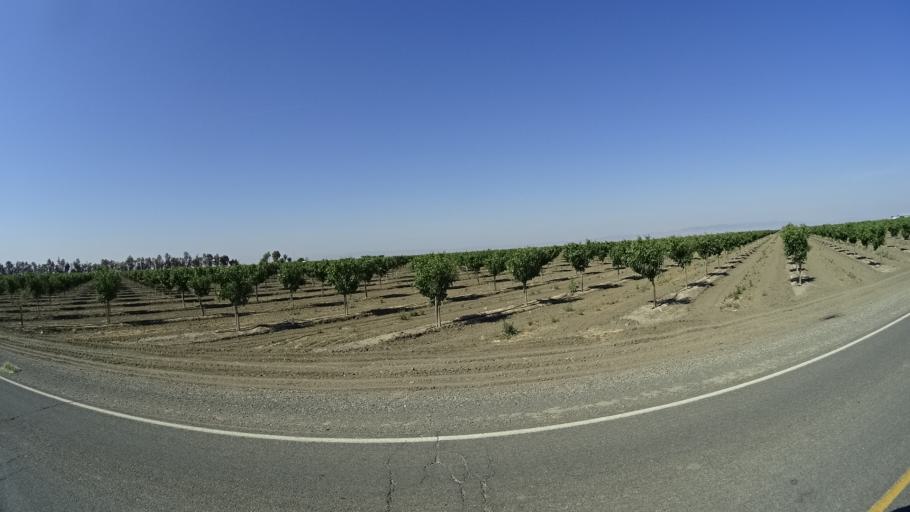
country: US
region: California
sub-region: Fresno County
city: Riverdale
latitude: 36.3844
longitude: -119.9391
